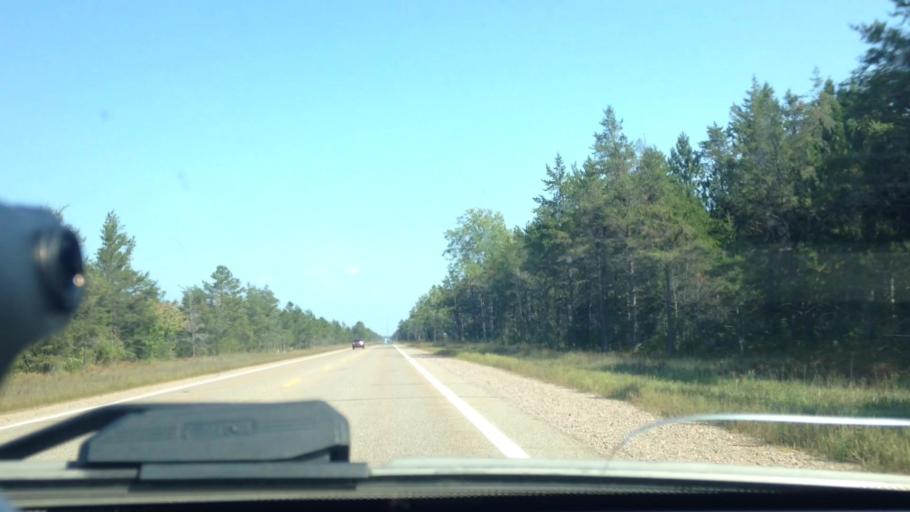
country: US
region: Michigan
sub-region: Mackinac County
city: Saint Ignace
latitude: 46.3585
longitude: -84.8519
